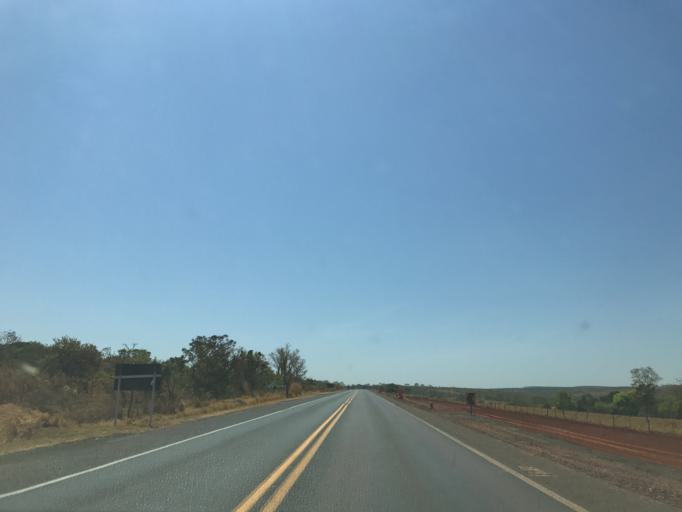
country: BR
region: Minas Gerais
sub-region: Prata
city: Prata
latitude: -19.4316
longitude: -48.8890
